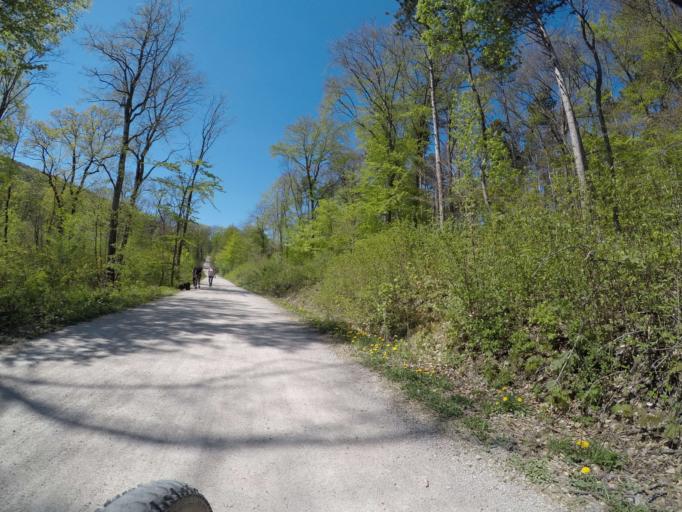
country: AT
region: Lower Austria
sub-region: Politischer Bezirk Modling
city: Gumpoldskirchen
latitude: 48.0630
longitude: 16.2590
